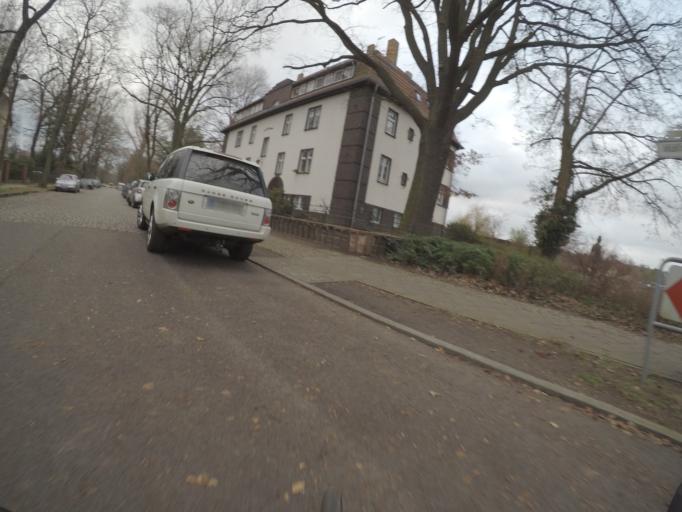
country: DE
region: Berlin
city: Grunau
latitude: 52.4140
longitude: 13.5905
